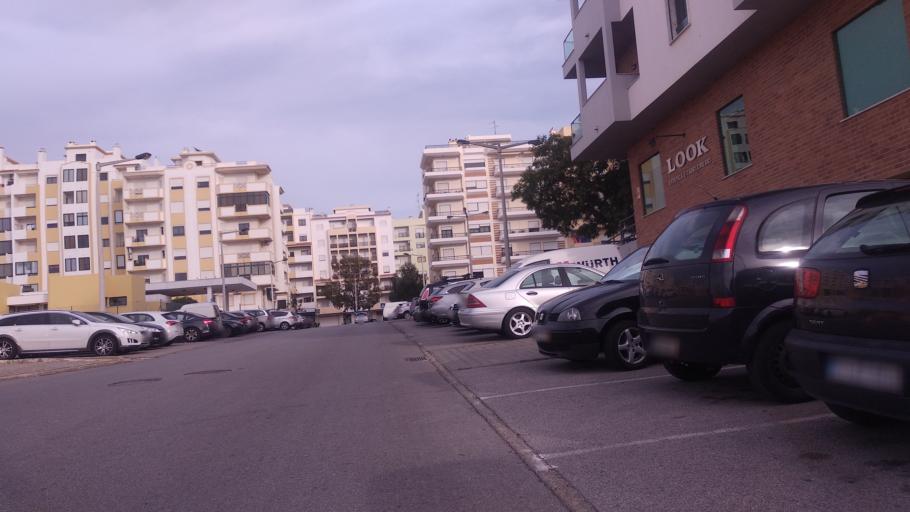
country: PT
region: Faro
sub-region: Faro
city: Faro
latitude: 37.0263
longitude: -7.9371
